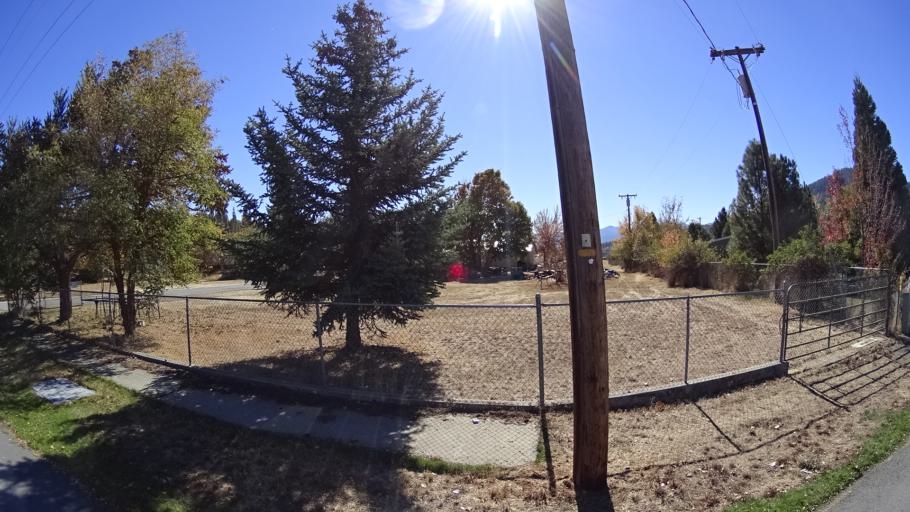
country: US
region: California
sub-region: Siskiyou County
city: Yreka
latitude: 41.6063
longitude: -122.8467
